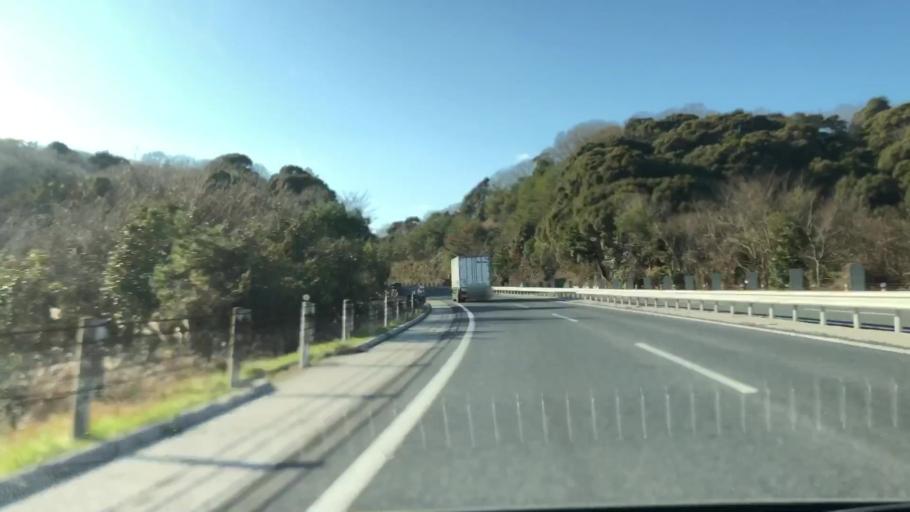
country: JP
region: Yamaguchi
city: Ogori-shimogo
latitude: 34.1815
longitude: 131.2882
